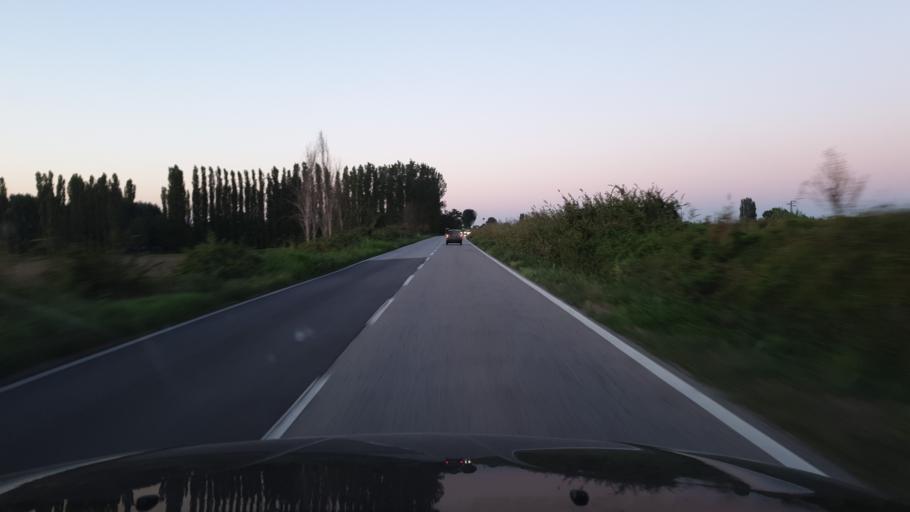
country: IT
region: Emilia-Romagna
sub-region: Provincia di Bologna
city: Altedo
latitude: 44.6524
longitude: 11.4844
